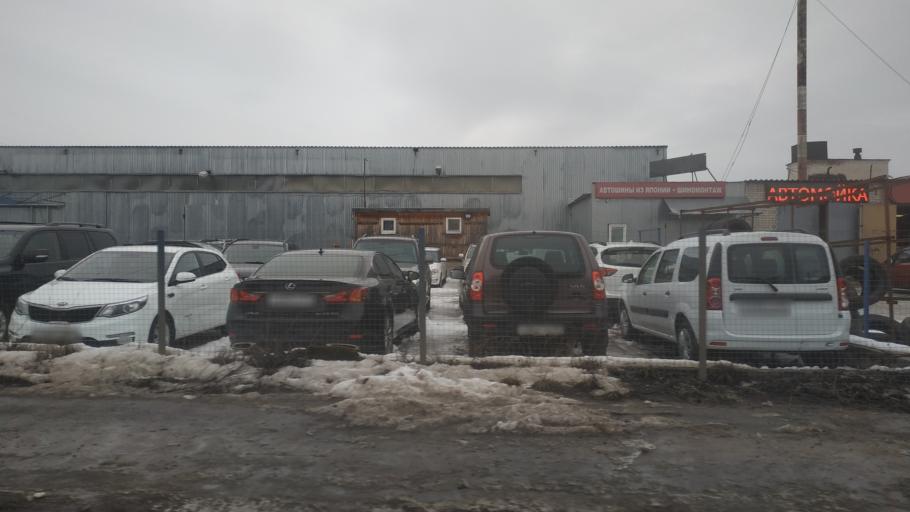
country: RU
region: Tverskaya
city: Tver
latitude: 56.8914
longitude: 35.8338
